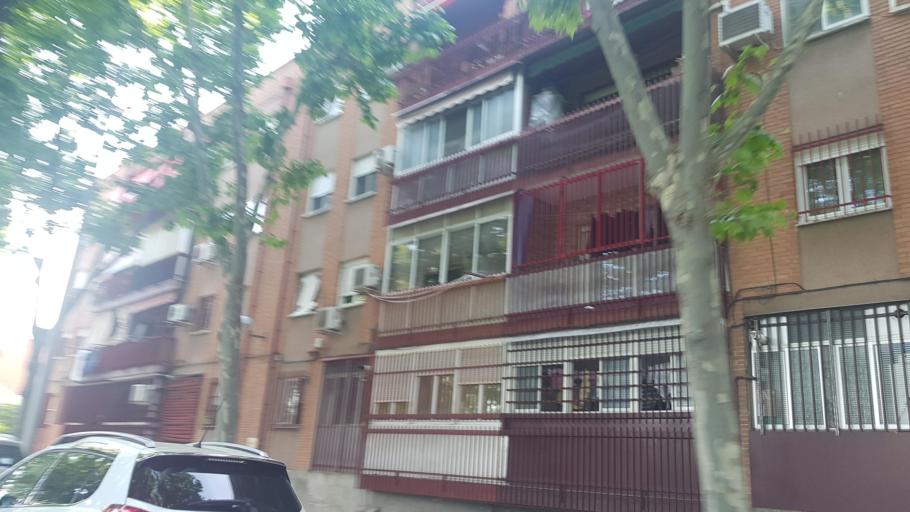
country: ES
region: Madrid
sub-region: Provincia de Madrid
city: Puente de Vallecas
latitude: 40.3715
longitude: -3.6571
